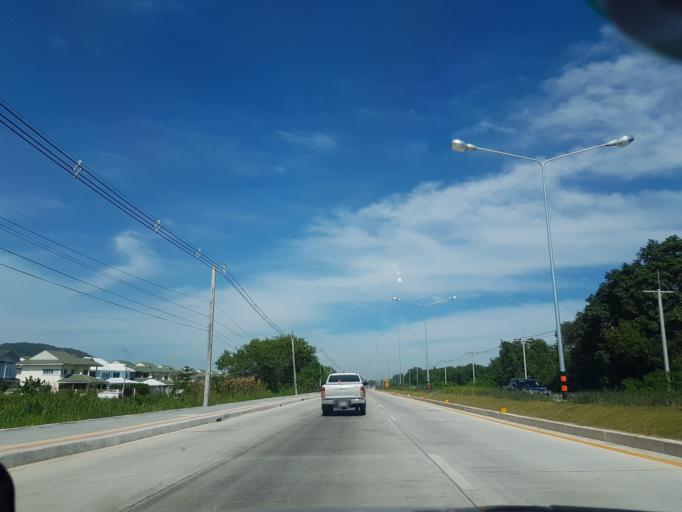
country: TH
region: Chon Buri
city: Sattahip
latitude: 12.6757
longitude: 100.9779
